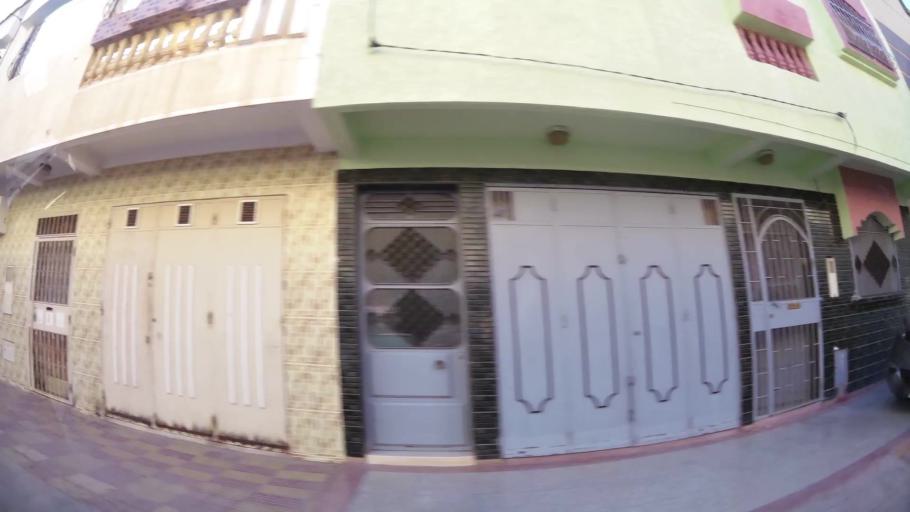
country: MA
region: Oriental
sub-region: Oujda-Angad
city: Oujda
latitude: 34.7076
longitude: -1.8955
